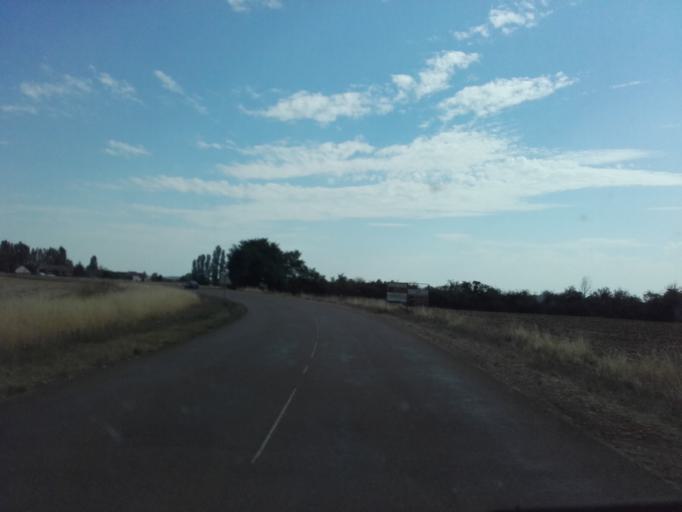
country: FR
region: Bourgogne
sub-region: Departement de la Cote-d'Or
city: Bligny-les-Beaune
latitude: 47.0030
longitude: 4.8508
